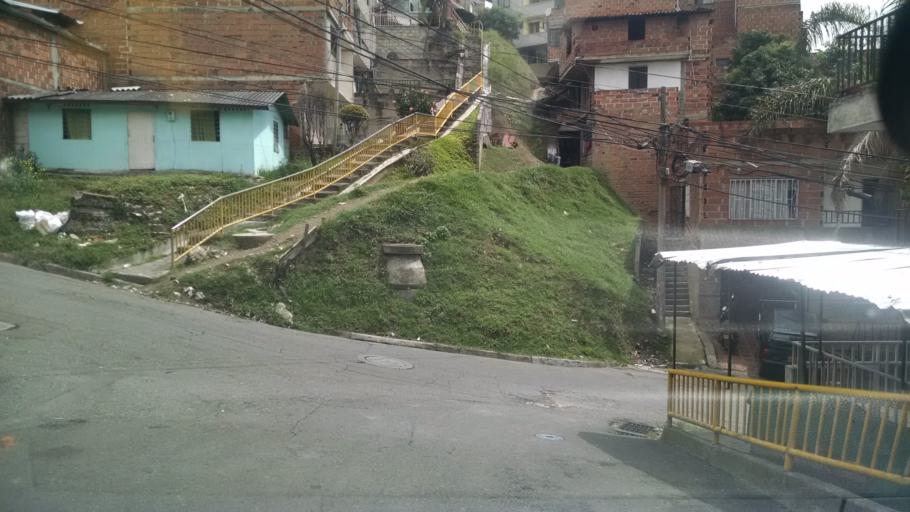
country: CO
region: Antioquia
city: Medellin
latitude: 6.2632
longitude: -75.6099
